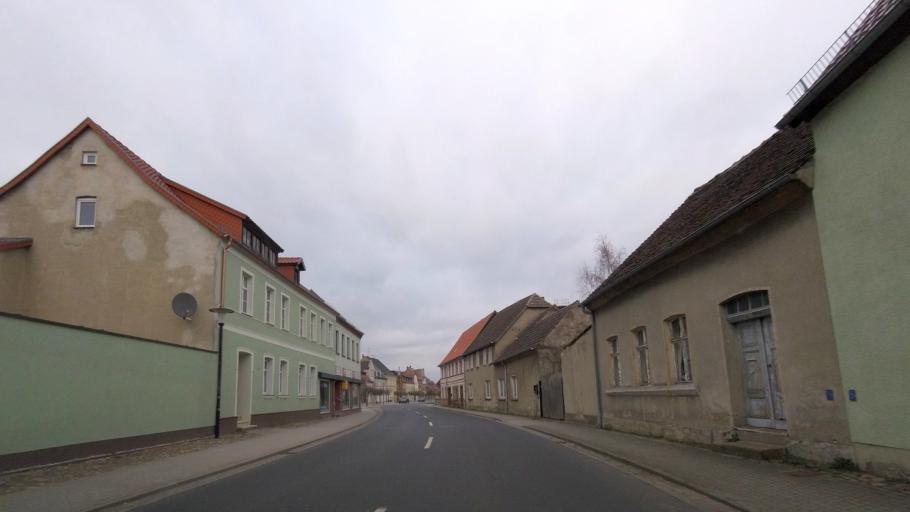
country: DE
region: Saxony-Anhalt
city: Kemberg
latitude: 51.7707
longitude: 12.6317
